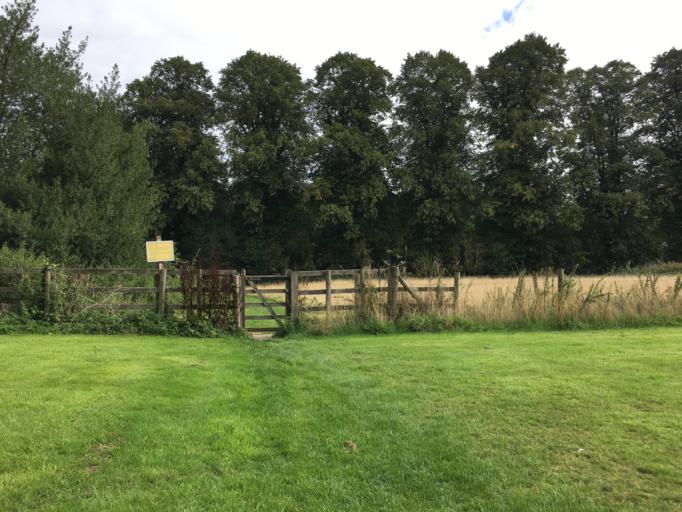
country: GB
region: England
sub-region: Warwickshire
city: Dunchurch
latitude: 52.3377
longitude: -1.2862
